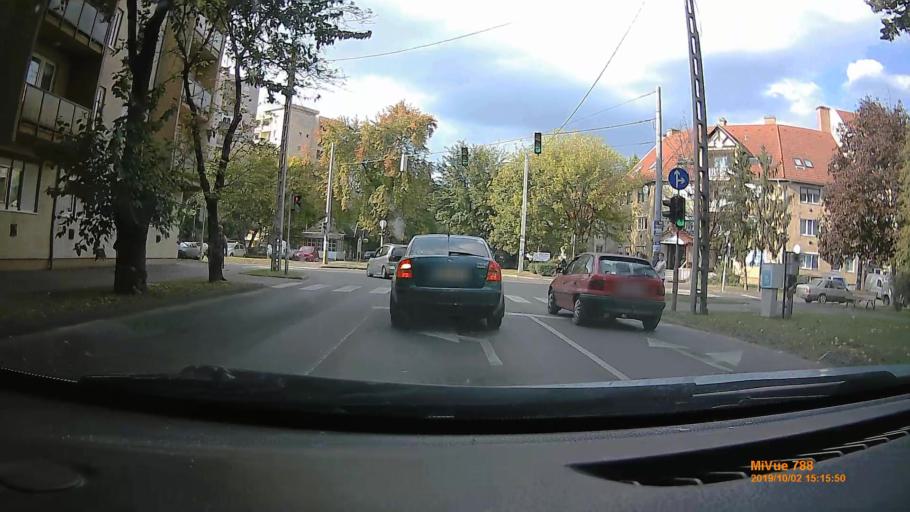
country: HU
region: Heves
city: Eger
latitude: 47.8953
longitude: 20.3877
